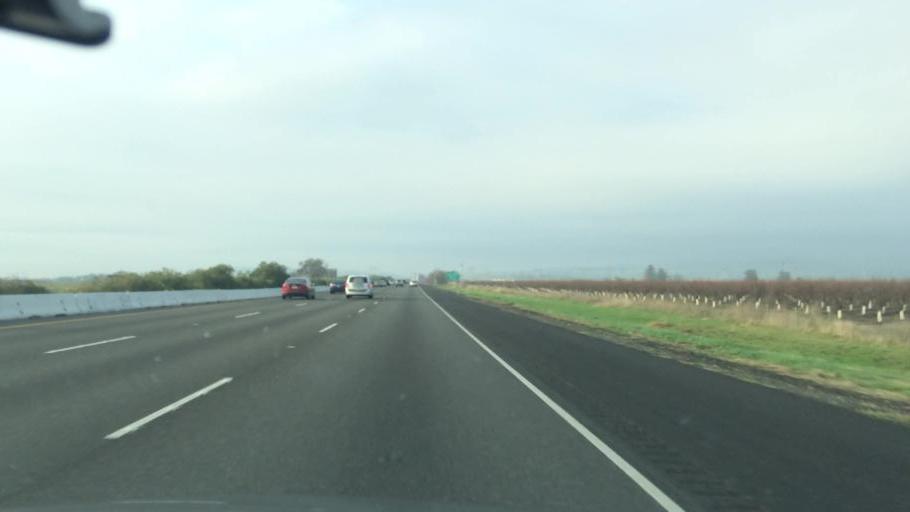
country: US
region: California
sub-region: Solano County
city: Hartley
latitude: 38.4129
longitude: -121.9020
